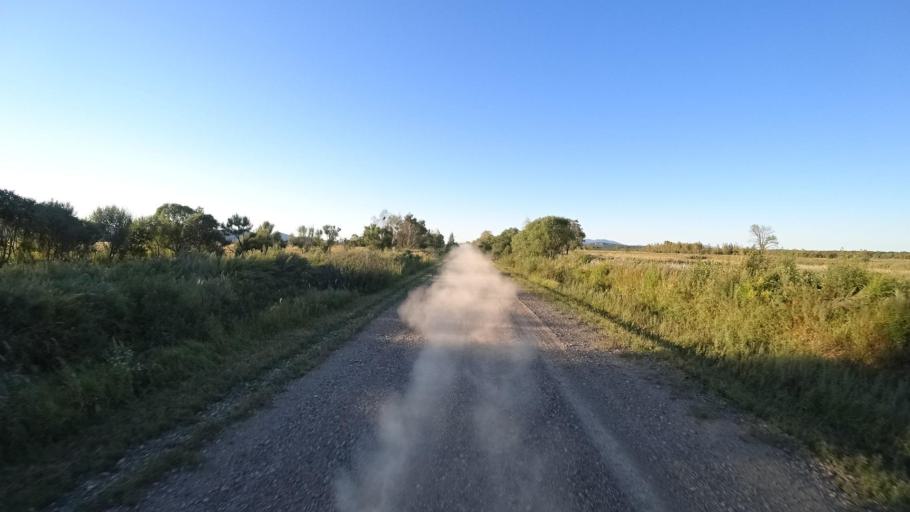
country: RU
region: Primorskiy
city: Kirovskiy
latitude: 44.7970
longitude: 133.6217
